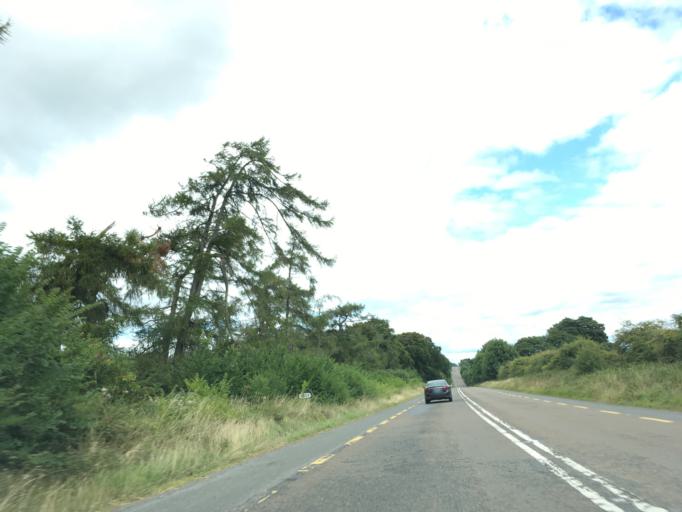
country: IE
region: Munster
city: Cashel
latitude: 52.4801
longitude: -7.8922
